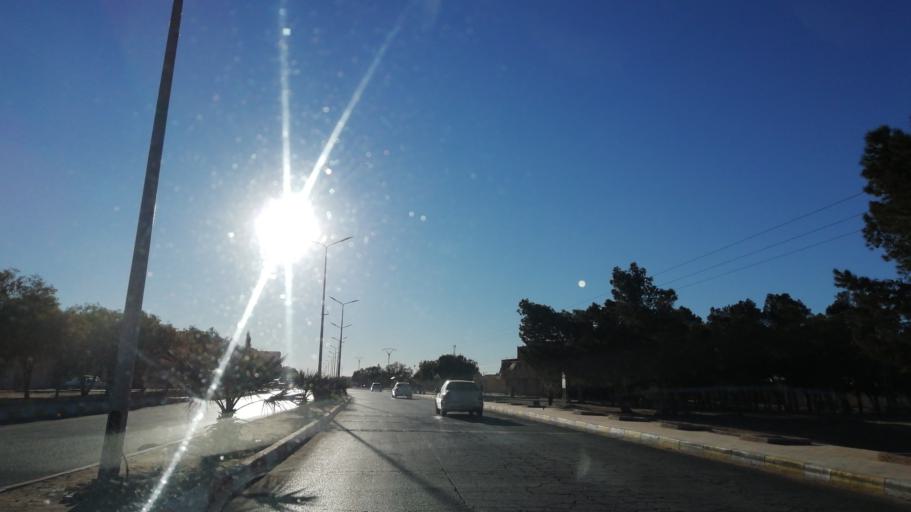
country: DZ
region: Saida
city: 'Ain el Hadjar
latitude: 34.0318
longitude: 0.0893
